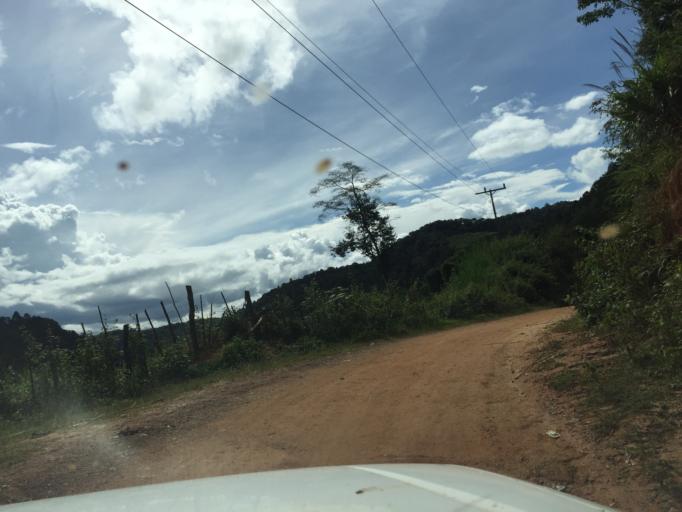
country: LA
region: Xiangkhoang
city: Muang Phonsavan
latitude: 19.3280
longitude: 103.4717
